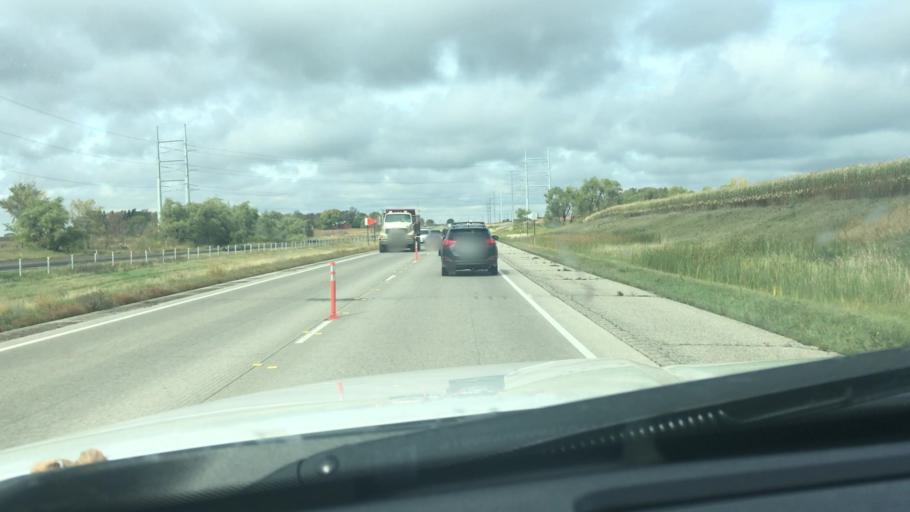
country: US
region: Minnesota
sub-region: Douglas County
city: Alexandria
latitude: 45.9173
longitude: -95.5542
